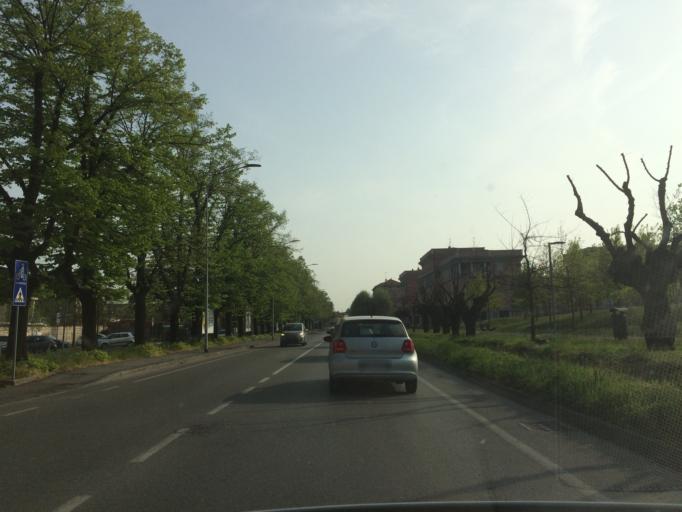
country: IT
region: Lombardy
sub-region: Provincia di Brescia
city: Brescia
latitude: 45.5275
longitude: 10.2325
